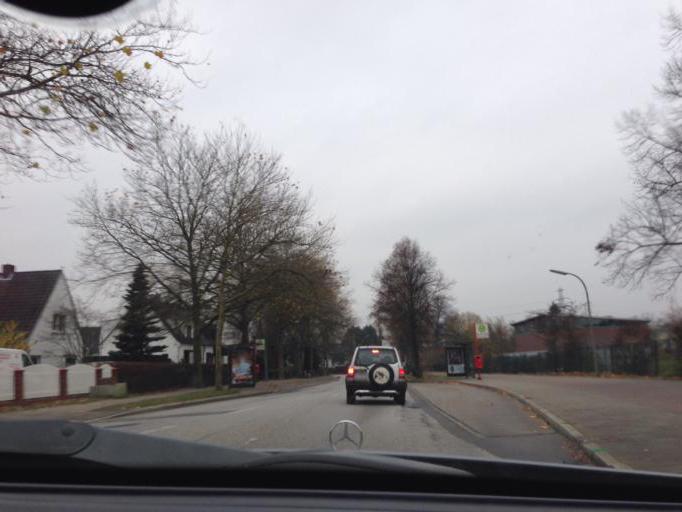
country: DE
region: Hamburg
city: Farmsen-Berne
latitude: 53.5999
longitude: 10.1324
